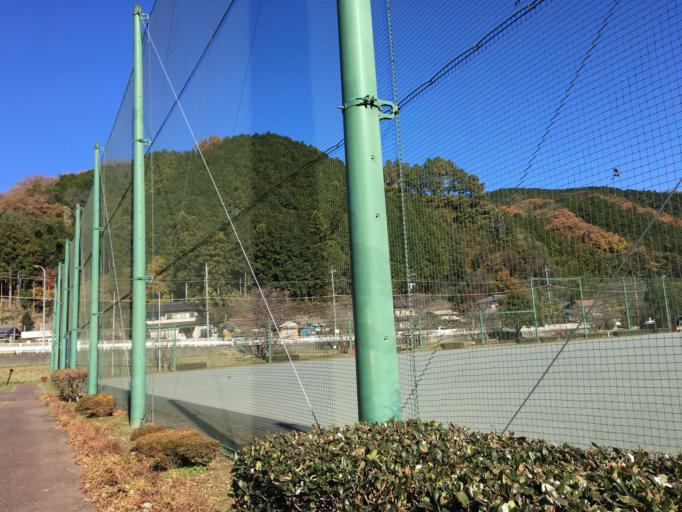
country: JP
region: Saitama
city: Yorii
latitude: 36.0555
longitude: 139.1995
